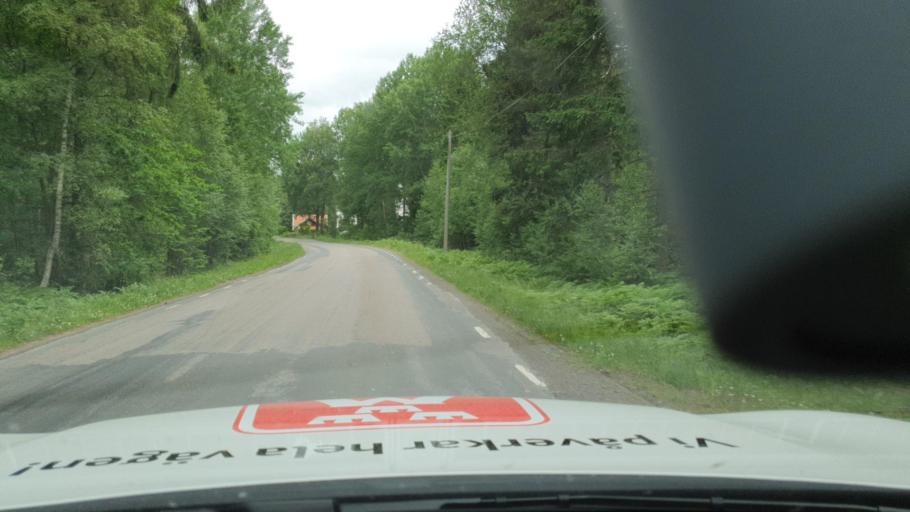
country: SE
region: Vaestra Goetaland
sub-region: Tidaholms Kommun
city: Olofstorp
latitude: 58.3274
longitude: 13.9962
